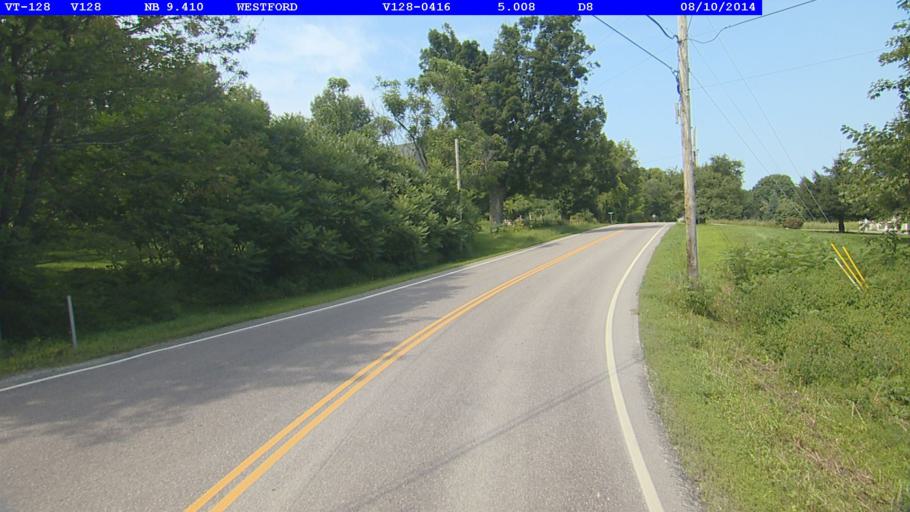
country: US
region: Vermont
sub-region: Chittenden County
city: Milton
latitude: 44.6255
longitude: -73.0201
